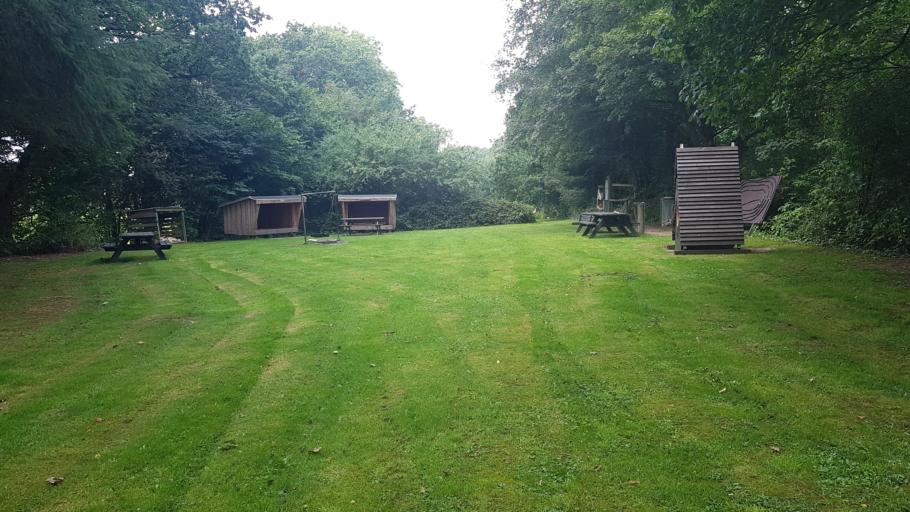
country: DK
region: South Denmark
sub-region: Aabenraa Kommune
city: Rodekro
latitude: 55.0584
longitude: 9.3419
